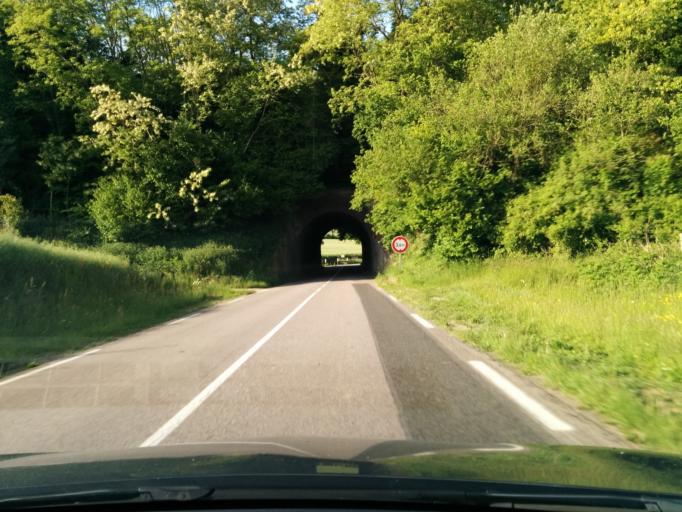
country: FR
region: Haute-Normandie
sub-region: Departement de l'Eure
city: Charleval
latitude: 49.3475
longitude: 1.4542
